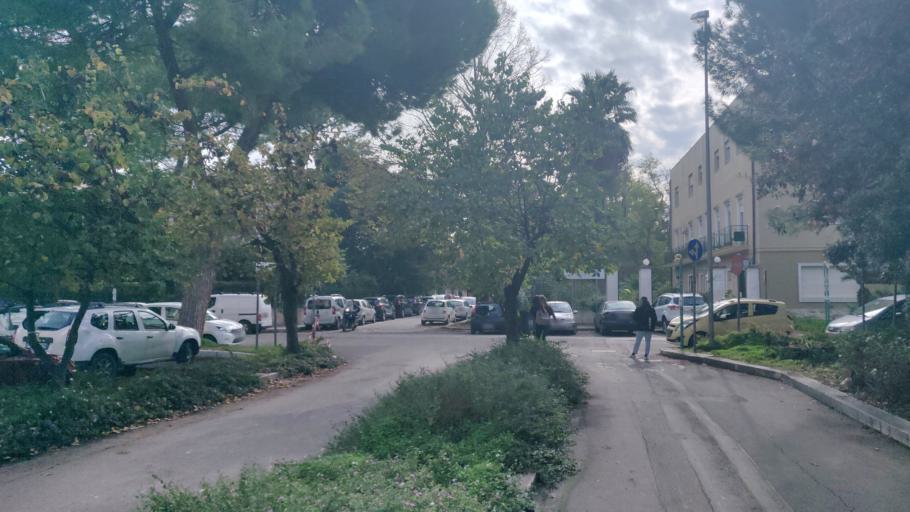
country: IT
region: Apulia
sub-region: Provincia di Bari
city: Bari
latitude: 41.1086
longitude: 16.8829
